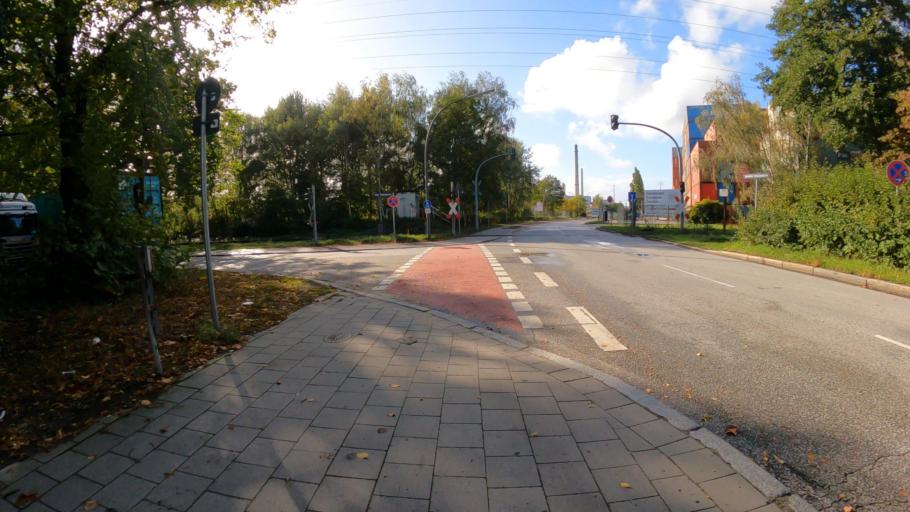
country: DE
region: Hamburg
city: Kleiner Grasbrook
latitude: 53.5122
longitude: 9.9668
